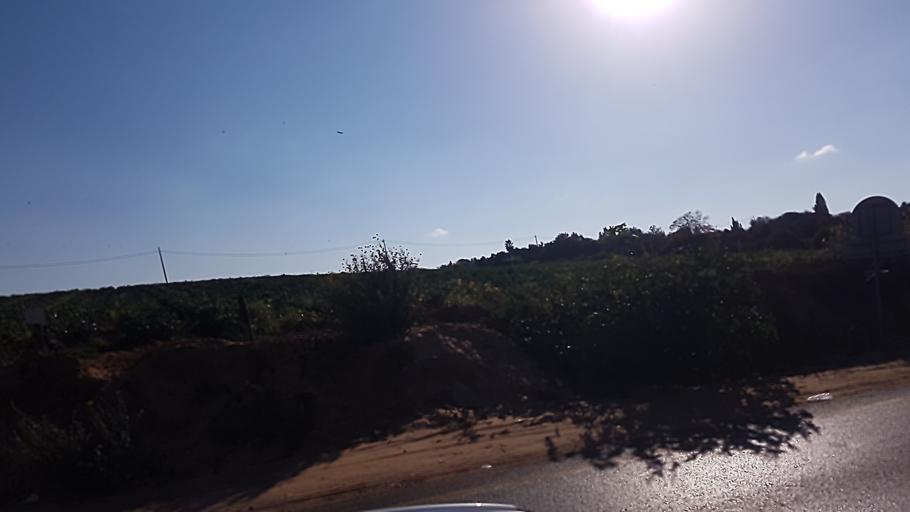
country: IL
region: Central District
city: Kfar Saba
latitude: 32.1977
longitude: 34.9224
